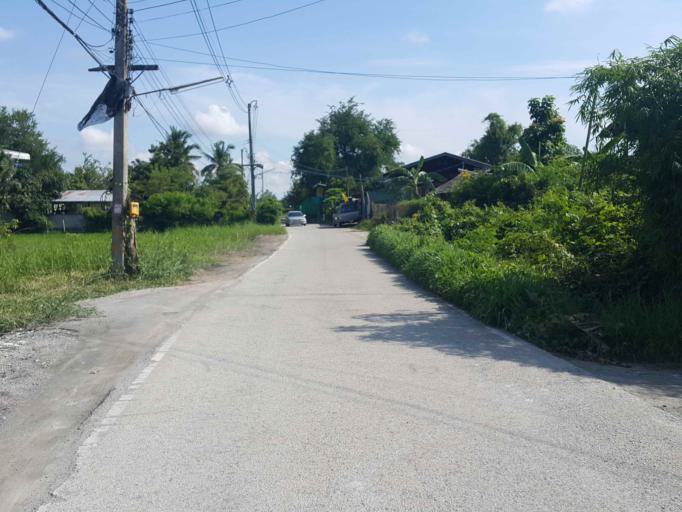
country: TH
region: Chiang Mai
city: San Kamphaeng
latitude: 18.7987
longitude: 99.1019
